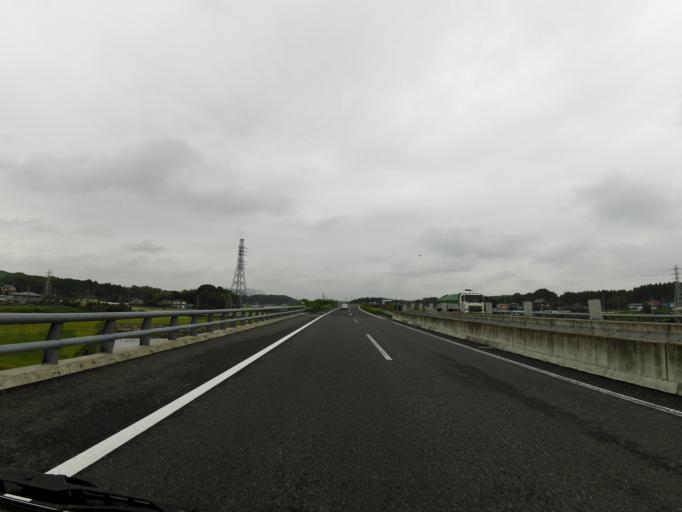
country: JP
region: Tochigi
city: Mooka
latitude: 36.4210
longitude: 139.9855
